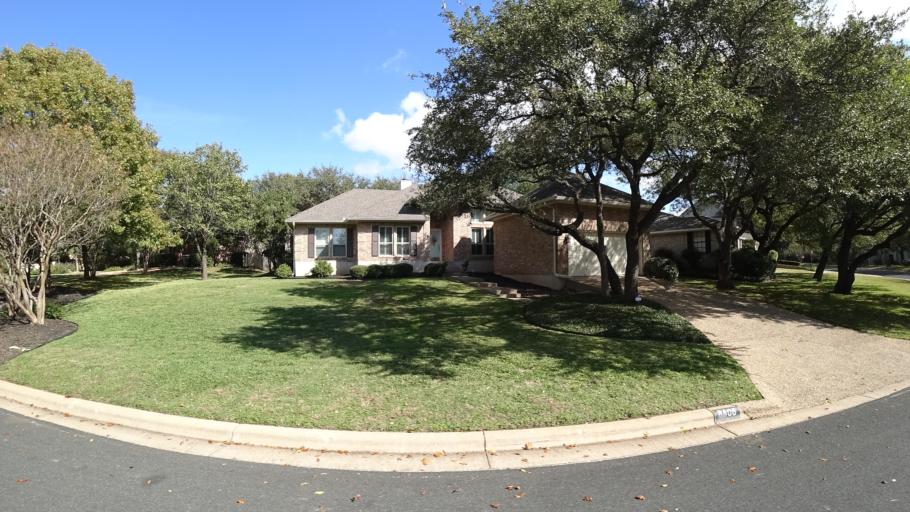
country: US
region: Texas
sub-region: Williamson County
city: Jollyville
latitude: 30.4215
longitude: -97.7876
